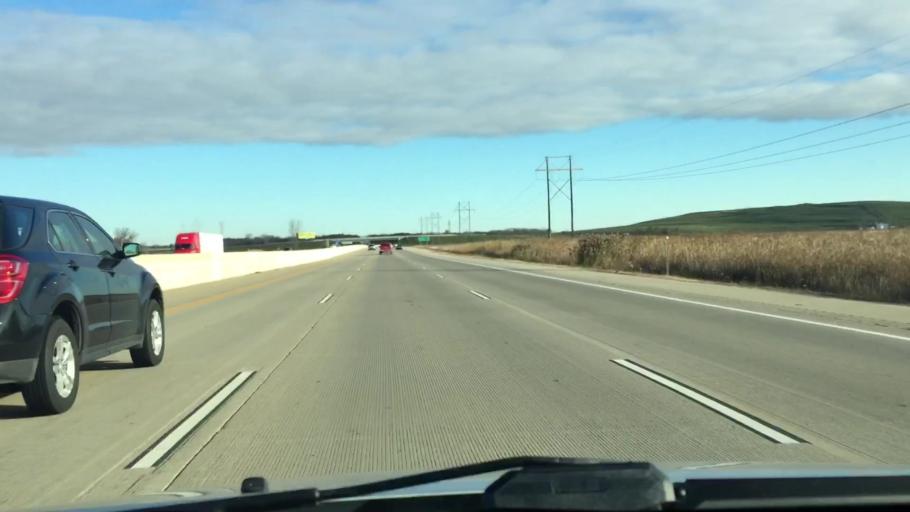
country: US
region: Wisconsin
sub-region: Winnebago County
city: Oshkosh
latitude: 44.0769
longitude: -88.5639
